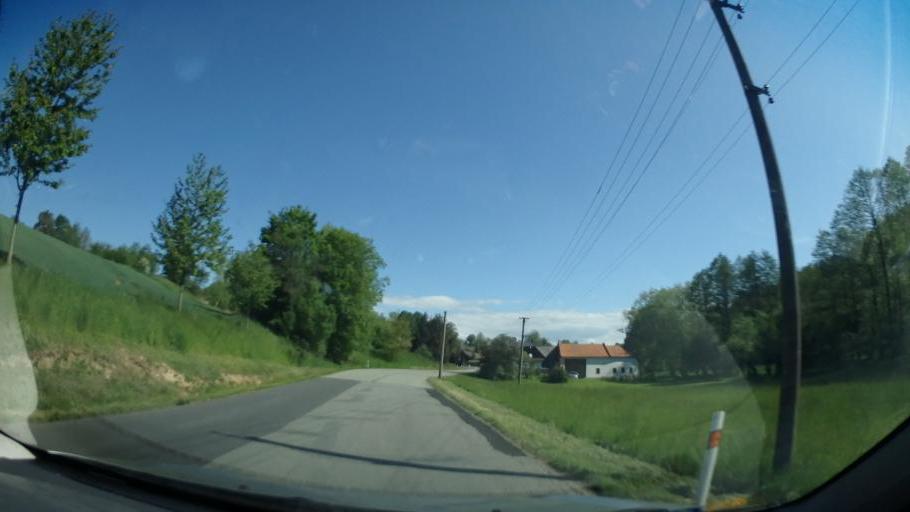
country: CZ
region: South Moravian
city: Velke Opatovice
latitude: 49.6587
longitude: 16.6296
